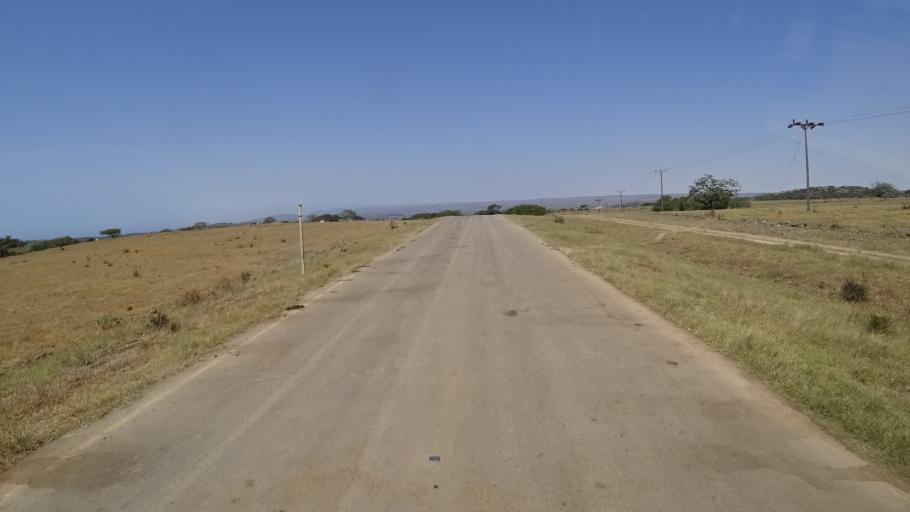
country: OM
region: Zufar
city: Salalah
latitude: 17.1216
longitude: 54.5885
